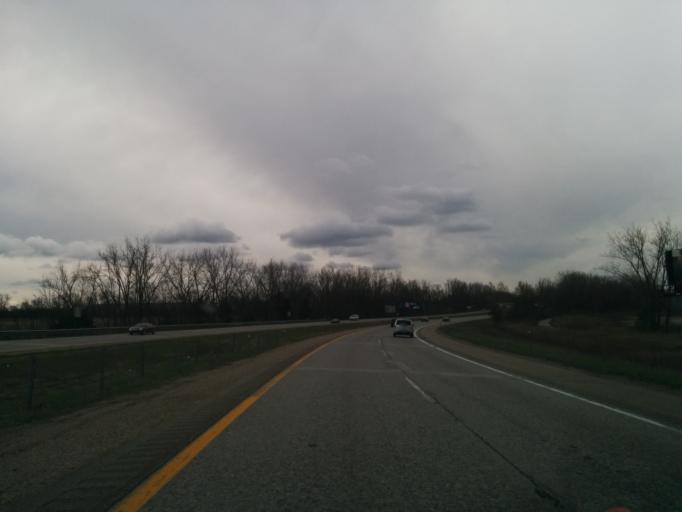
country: US
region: Michigan
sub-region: Kent County
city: Grand Rapids
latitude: 42.9538
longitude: -85.7055
